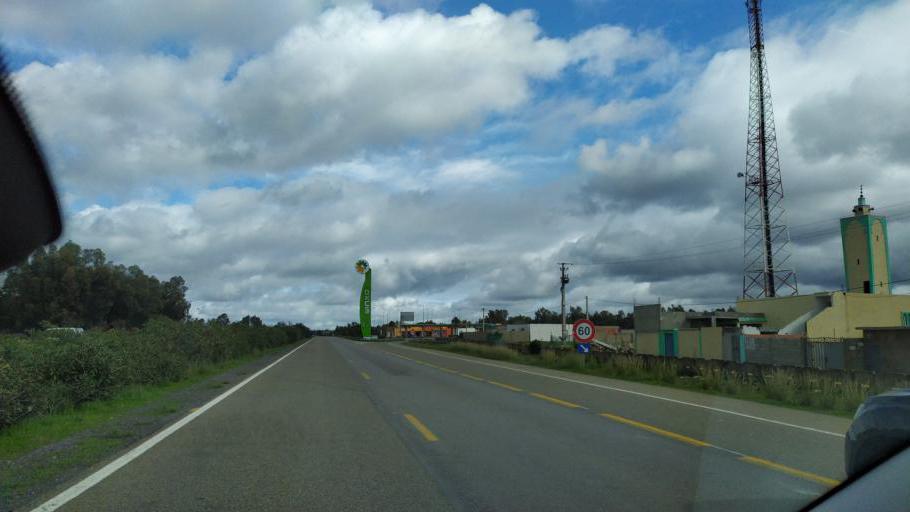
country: MA
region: Gharb-Chrarda-Beni Hssen
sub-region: Kenitra Province
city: Lalla Mimouna
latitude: 34.8728
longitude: -6.2157
